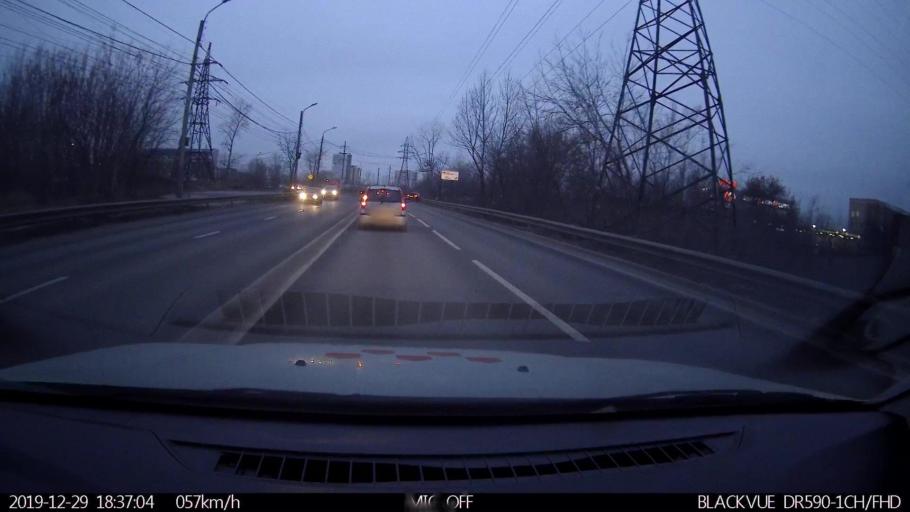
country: RU
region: Nizjnij Novgorod
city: Neklyudovo
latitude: 56.3447
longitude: 43.8910
